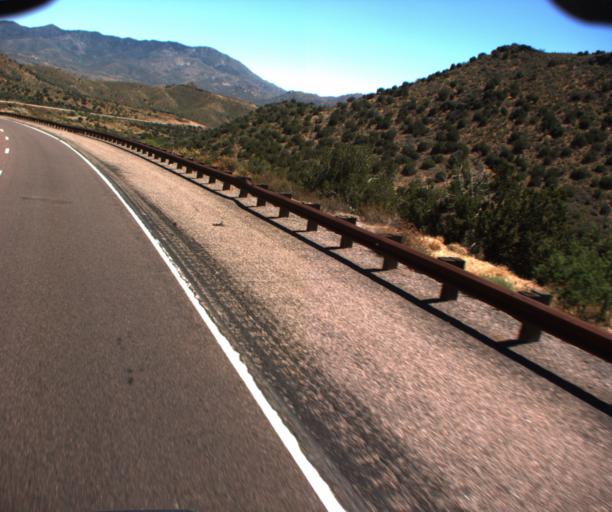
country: US
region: Arizona
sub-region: Gila County
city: Tonto Basin
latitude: 33.8957
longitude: -111.4578
